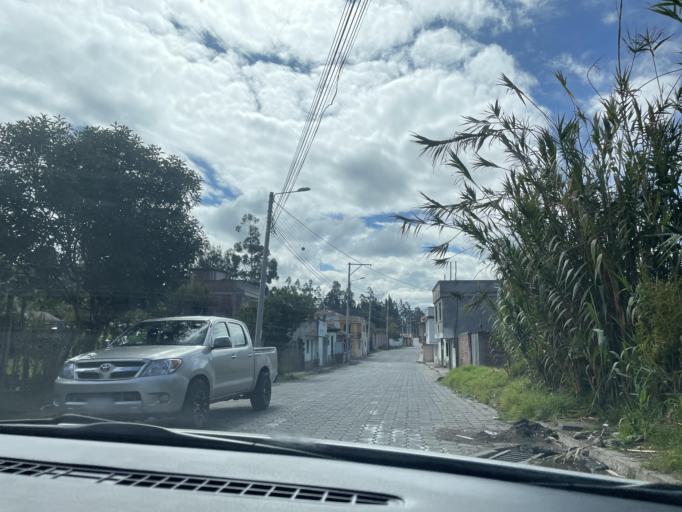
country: EC
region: Chimborazo
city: Guano
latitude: -1.6069
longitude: -78.6240
